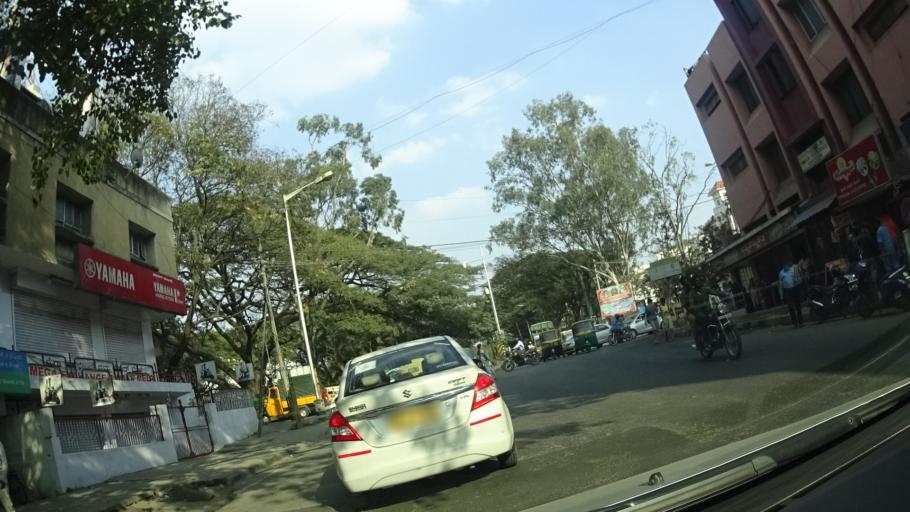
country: IN
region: Karnataka
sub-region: Bangalore Urban
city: Bangalore
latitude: 12.9573
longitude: 77.5717
